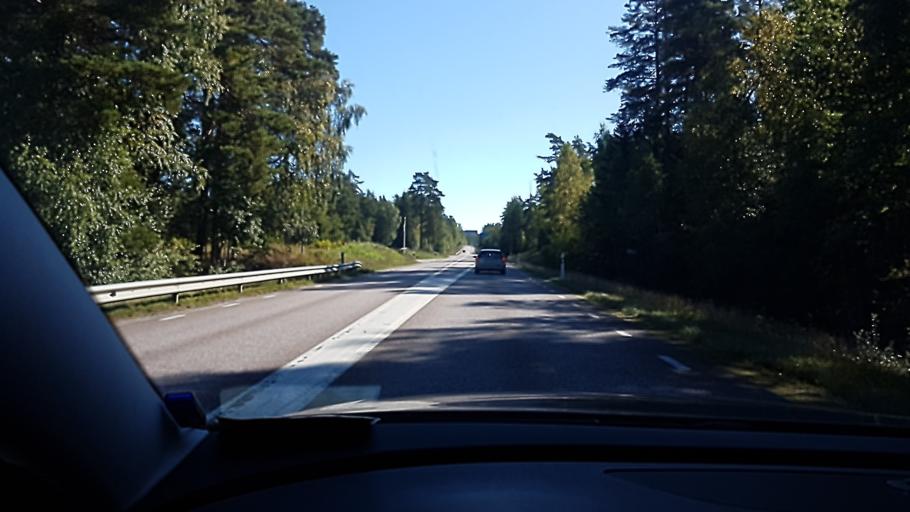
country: SE
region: Kronoberg
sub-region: Lessebo Kommun
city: Lessebo
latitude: 56.7820
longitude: 15.2282
